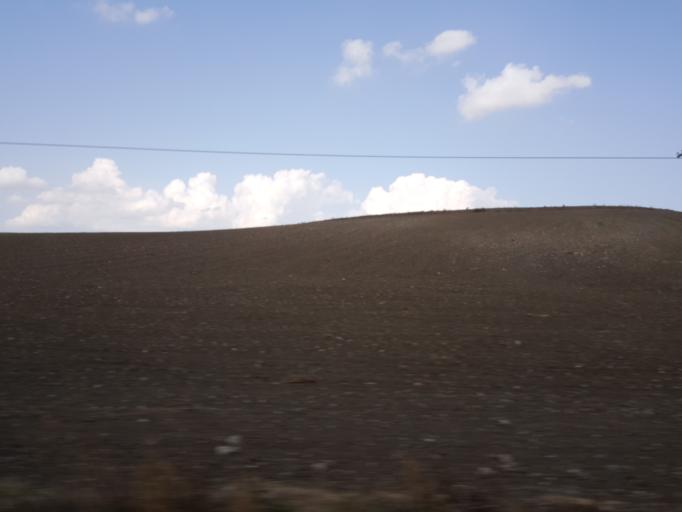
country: TR
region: Corum
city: Bogazkale
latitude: 40.1312
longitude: 34.5453
